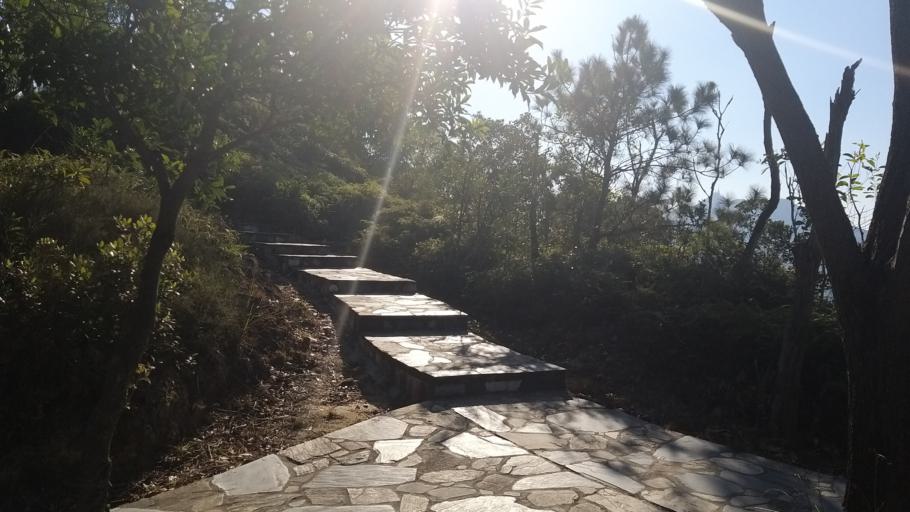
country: HK
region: Tuen Mun
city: Tuen Mun
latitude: 22.4026
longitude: 113.9885
